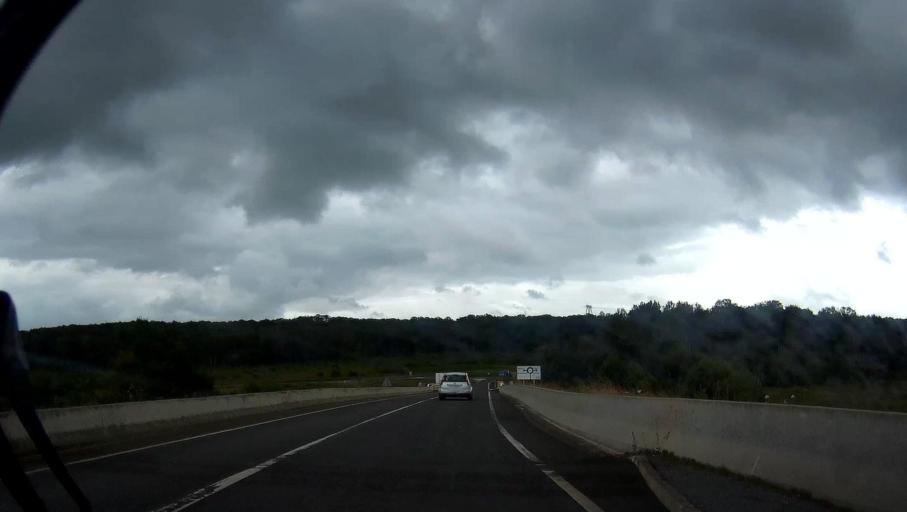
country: FR
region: Champagne-Ardenne
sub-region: Departement des Ardennes
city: Tournes
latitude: 49.7643
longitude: 4.6419
